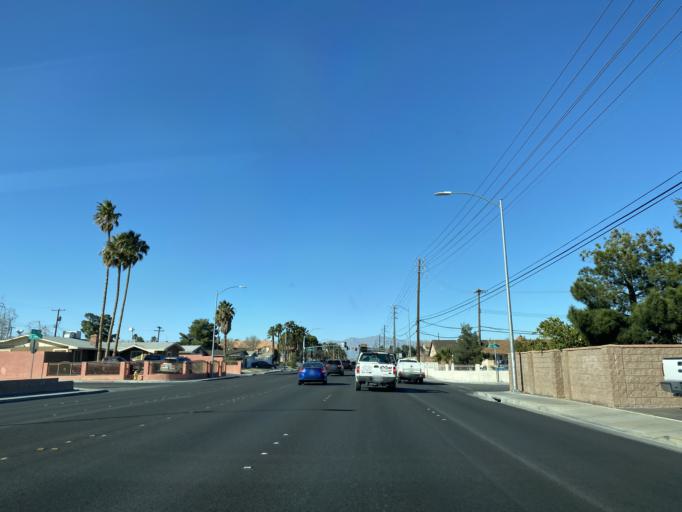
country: US
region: Nevada
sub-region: Clark County
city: Las Vegas
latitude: 36.1499
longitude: -115.1907
